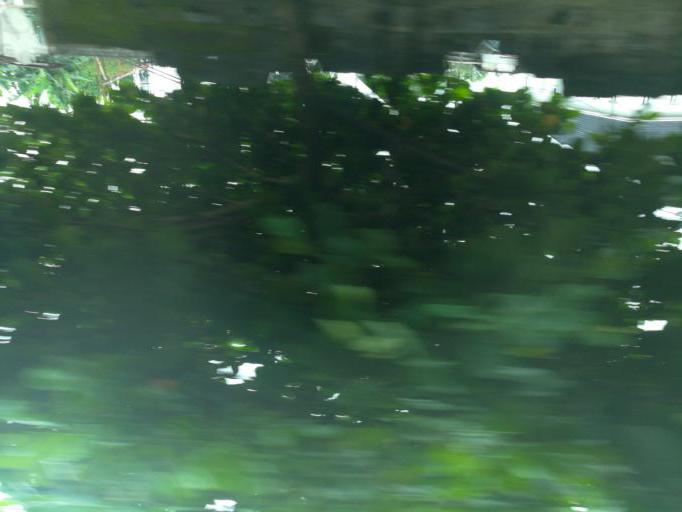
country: NG
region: Rivers
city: Port Harcourt
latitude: 4.8294
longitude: 7.0228
